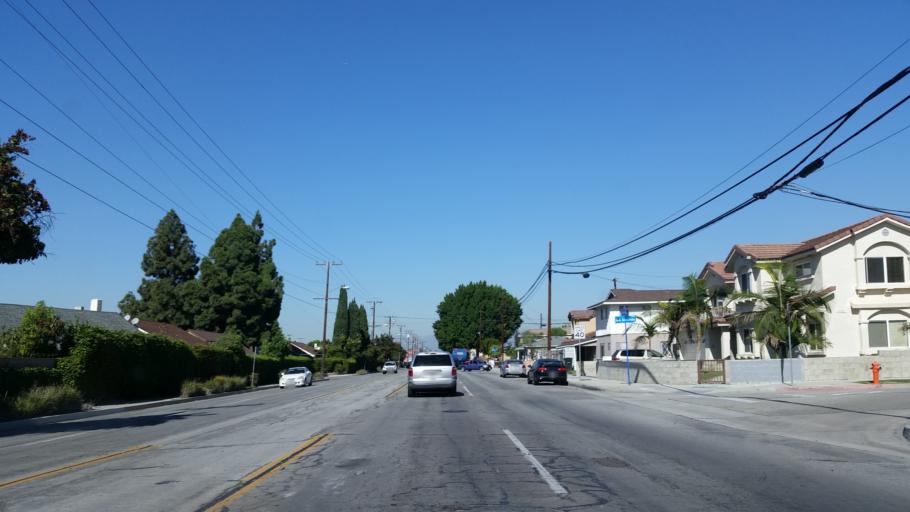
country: US
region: California
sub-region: Los Angeles County
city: Cerritos
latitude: 33.8546
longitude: -118.0723
